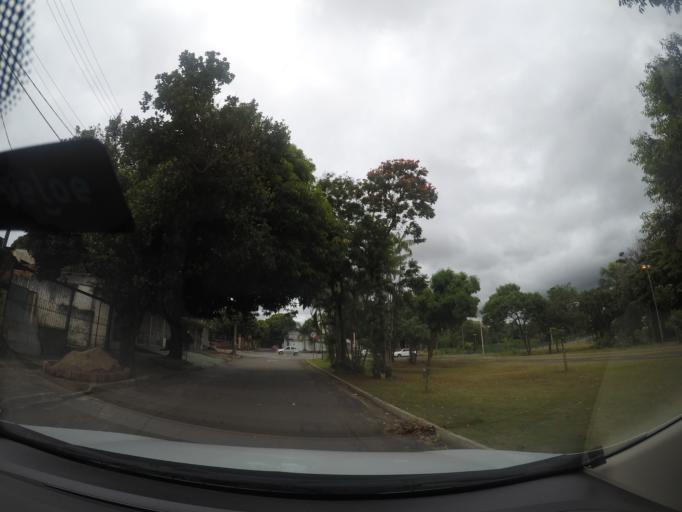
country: BR
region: Goias
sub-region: Goiania
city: Goiania
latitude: -16.7156
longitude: -49.3204
